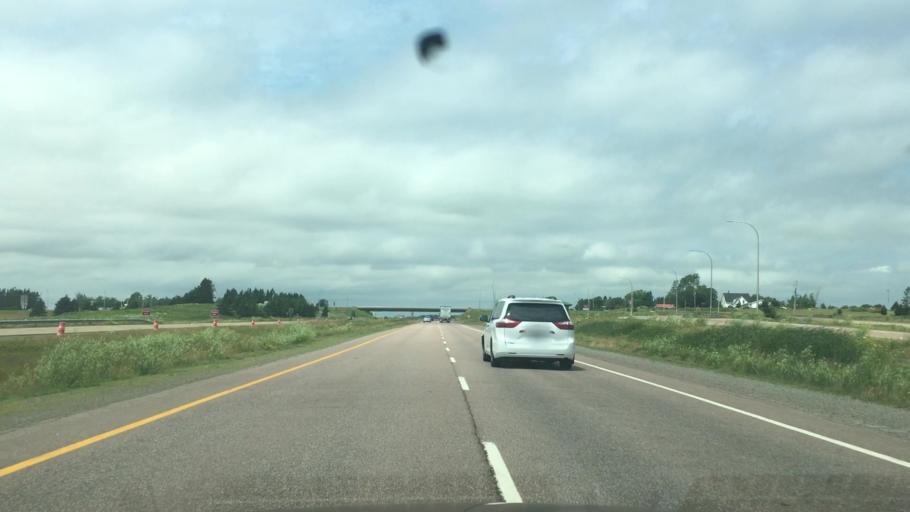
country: CA
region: Nova Scotia
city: Amherst
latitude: 45.8505
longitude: -64.2497
